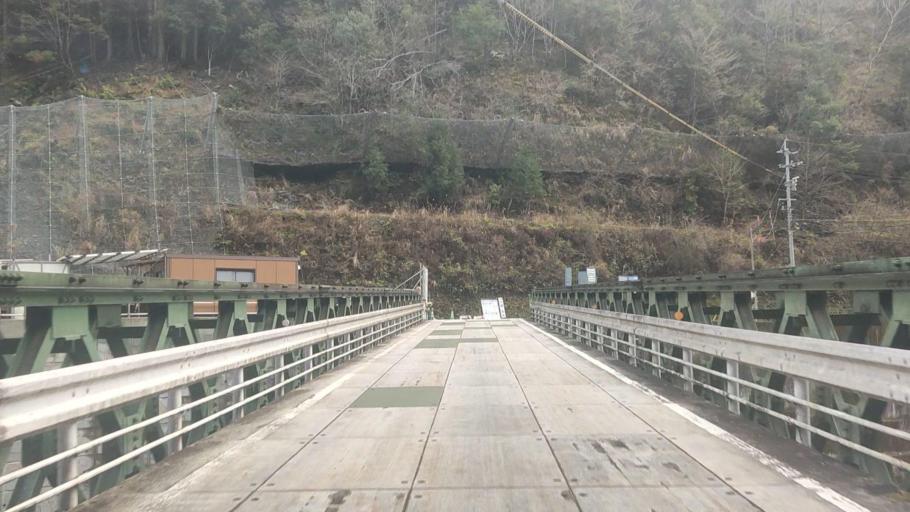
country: JP
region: Kumamoto
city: Matsubase
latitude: 32.4803
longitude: 130.8888
